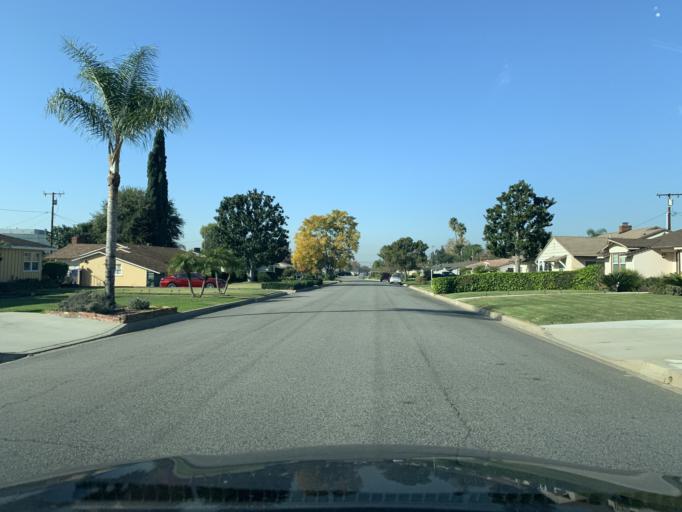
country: US
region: California
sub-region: Los Angeles County
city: Covina
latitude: 34.0768
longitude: -117.8775
